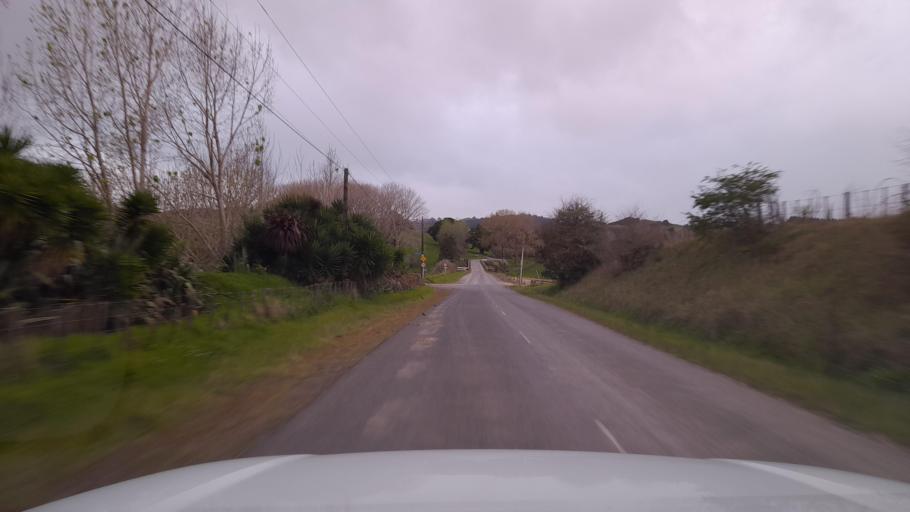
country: NZ
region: Northland
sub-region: Whangarei
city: Maungatapere
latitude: -35.6336
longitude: 174.2017
